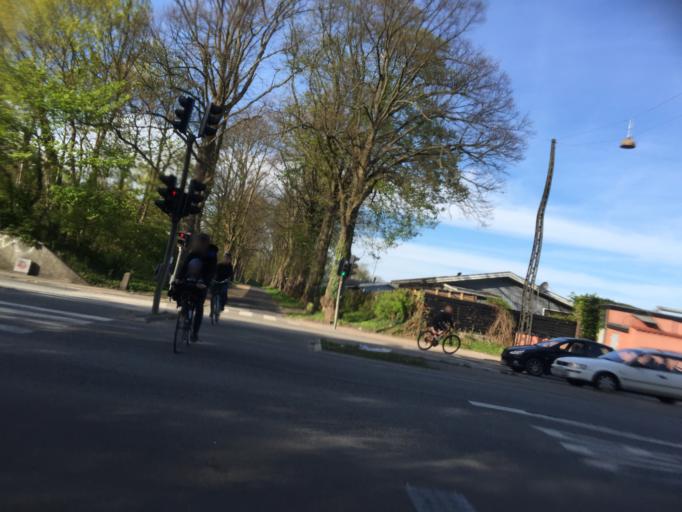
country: DK
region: Capital Region
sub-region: Herlev Kommune
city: Herlev
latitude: 55.7135
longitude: 12.4660
